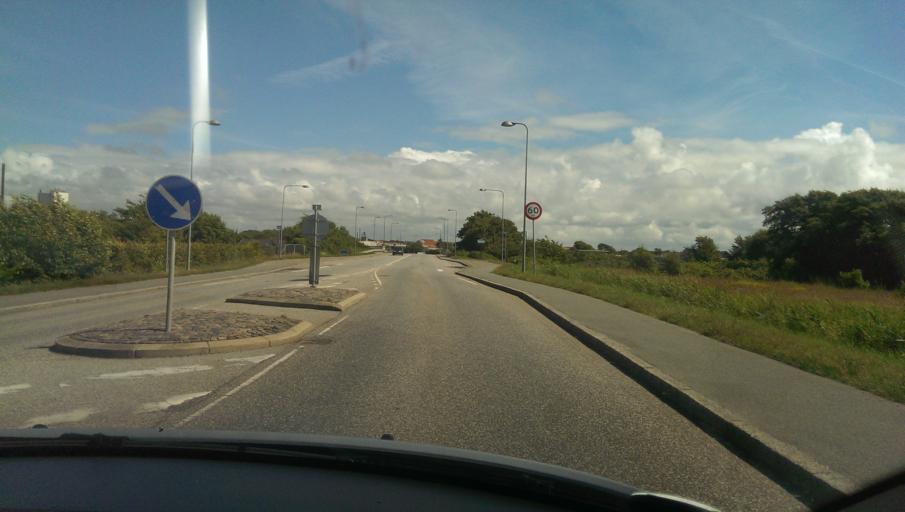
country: DK
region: Central Jutland
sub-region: Ringkobing-Skjern Kommune
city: Ringkobing
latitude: 56.0965
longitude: 8.2307
